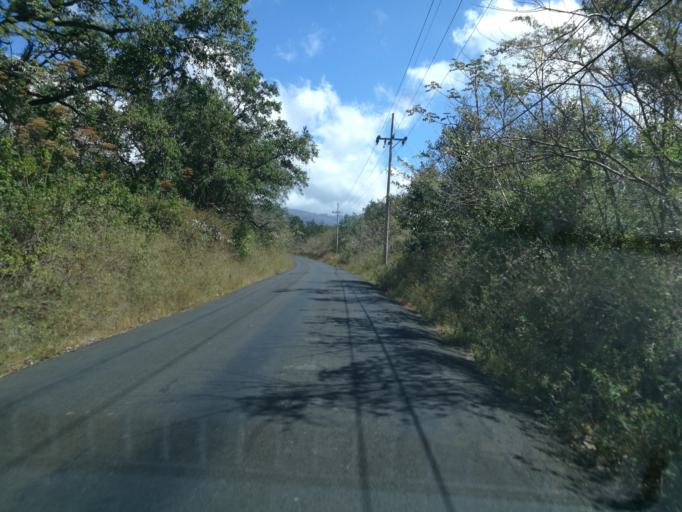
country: CR
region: Guanacaste
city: Liberia
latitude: 10.7424
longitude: -85.3850
